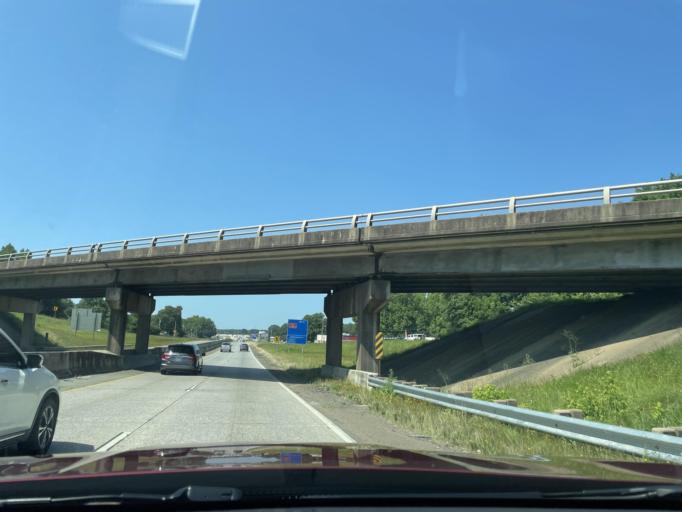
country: US
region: Arkansas
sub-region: Pulaski County
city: Jacksonville
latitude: 34.8756
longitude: -92.1181
